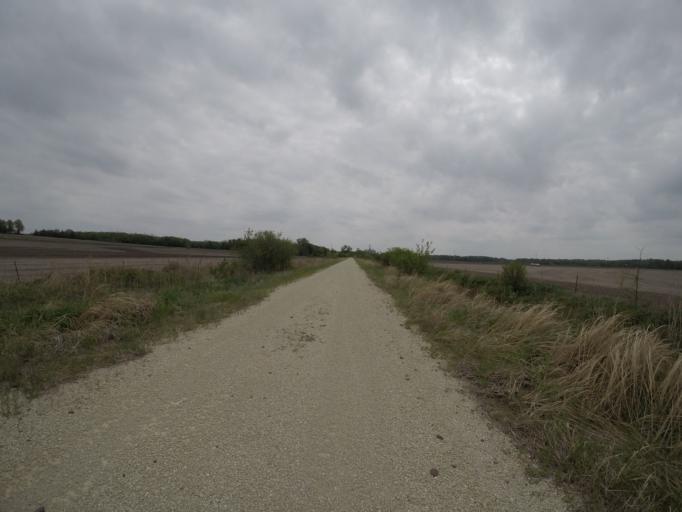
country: US
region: Nebraska
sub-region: Gage County
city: Wymore
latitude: 40.0615
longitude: -96.5798
